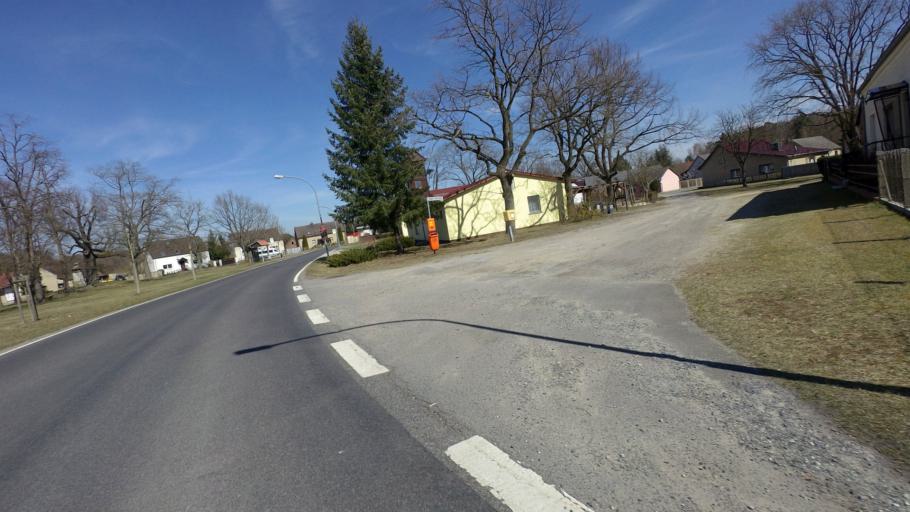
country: DE
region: Brandenburg
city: Storkow
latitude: 52.1936
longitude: 13.9185
